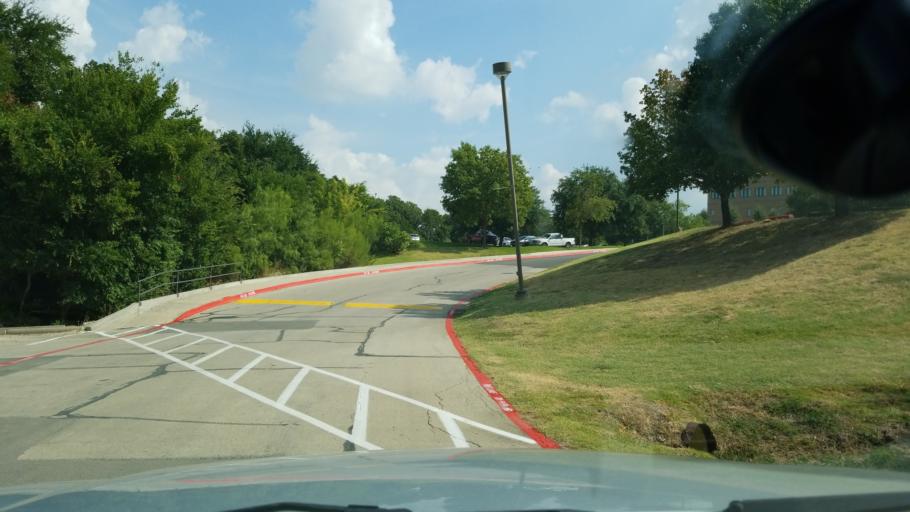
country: US
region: Texas
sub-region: Dallas County
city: Irving
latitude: 32.8468
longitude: -96.9220
